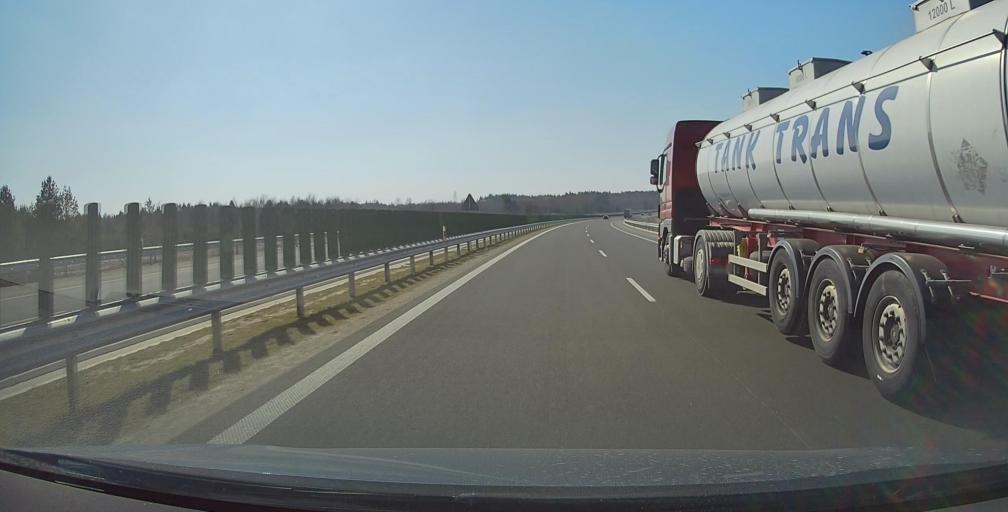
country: PL
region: Subcarpathian Voivodeship
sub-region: Powiat nizanski
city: Konczyce
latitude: 50.4371
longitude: 22.1391
